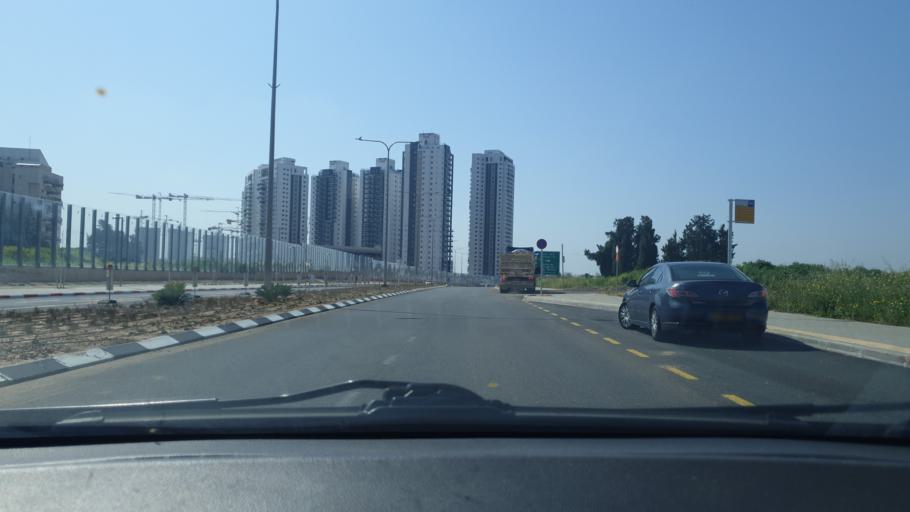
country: IL
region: Central District
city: Ramla
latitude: 31.9372
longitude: 34.8526
